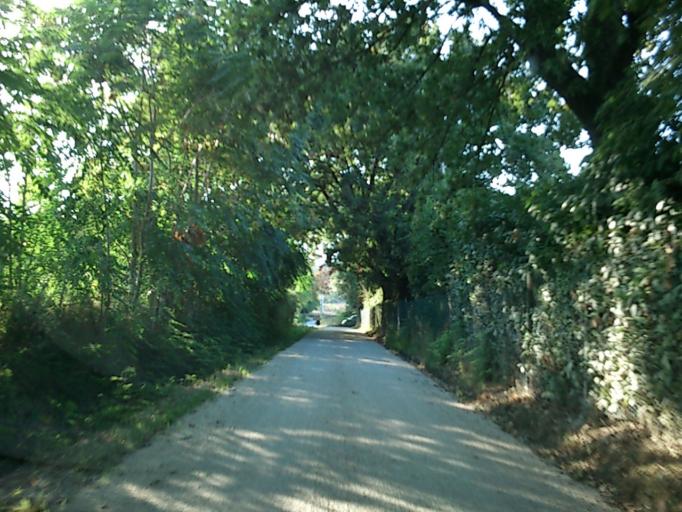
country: IT
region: The Marches
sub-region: Provincia di Pesaro e Urbino
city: Calcinelli
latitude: 43.7616
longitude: 12.9183
